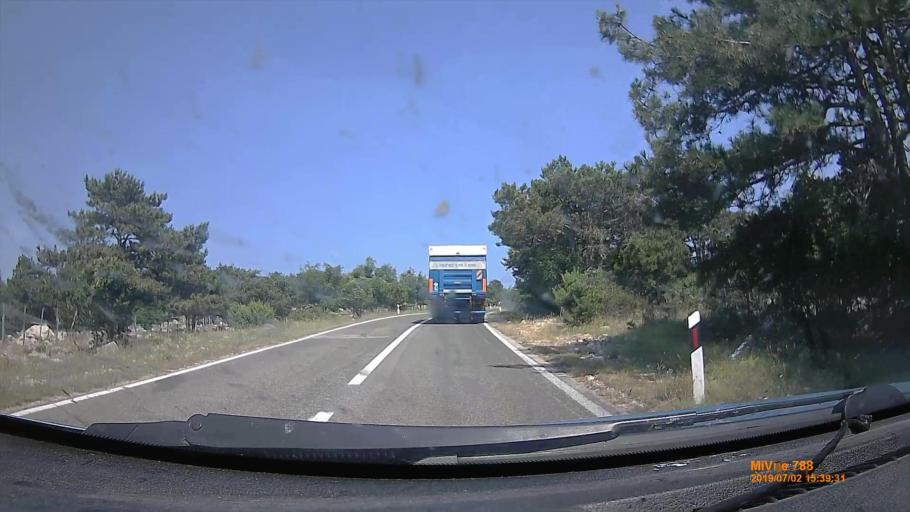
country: HR
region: Primorsko-Goranska
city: Cres
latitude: 44.9711
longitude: 14.4264
